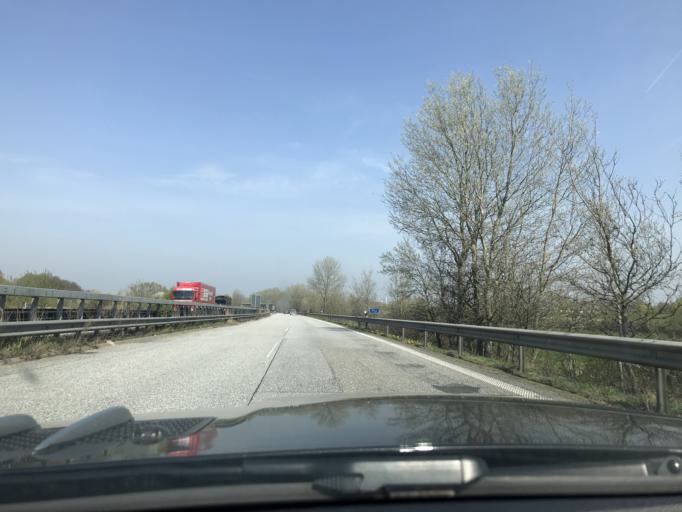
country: DE
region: Schleswig-Holstein
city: Altenkrempe
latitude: 54.1332
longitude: 10.8365
